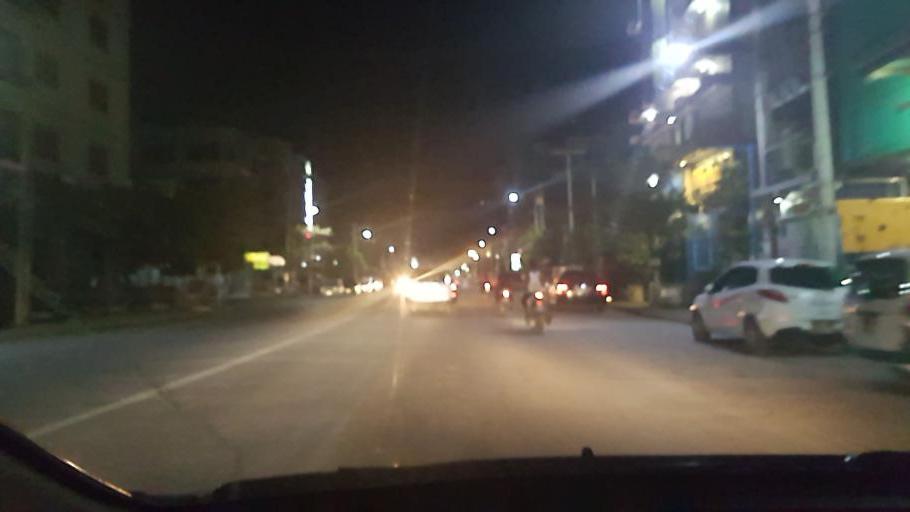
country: MM
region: Mandalay
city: Mandalay
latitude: 21.9774
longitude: 96.0956
